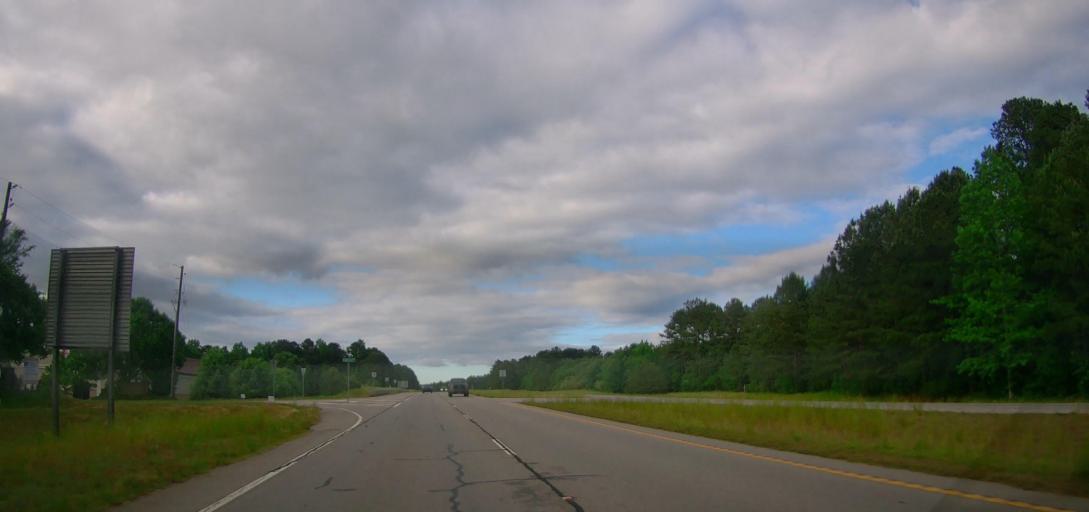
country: US
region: Georgia
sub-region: Oconee County
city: Watkinsville
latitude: 33.8757
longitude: -83.4186
